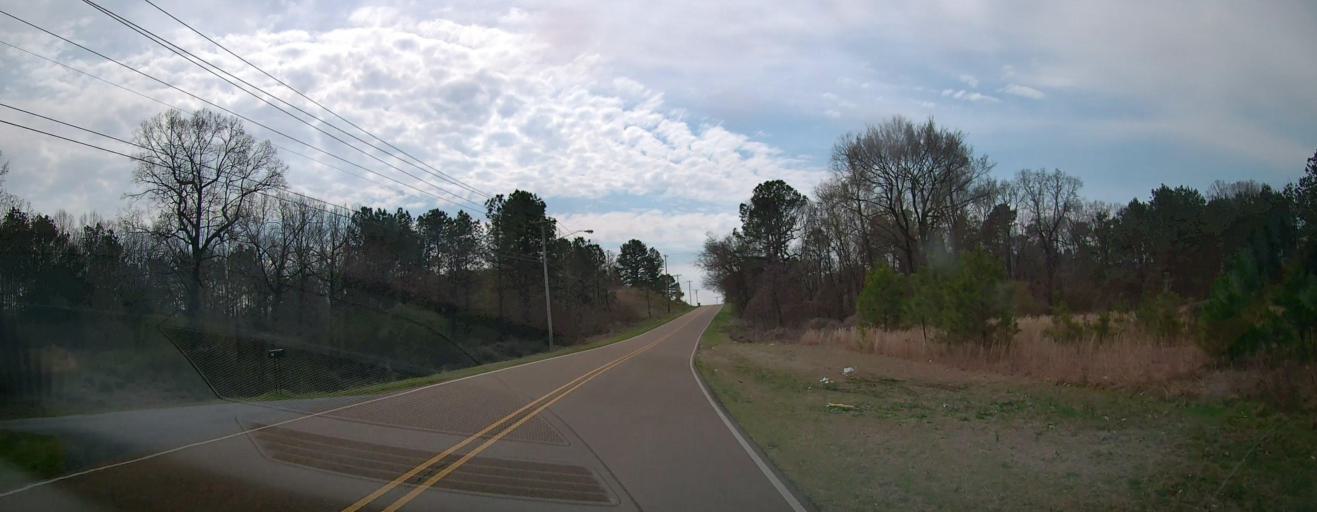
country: US
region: Mississippi
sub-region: Marshall County
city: Holly Springs
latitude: 34.7573
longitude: -89.4294
